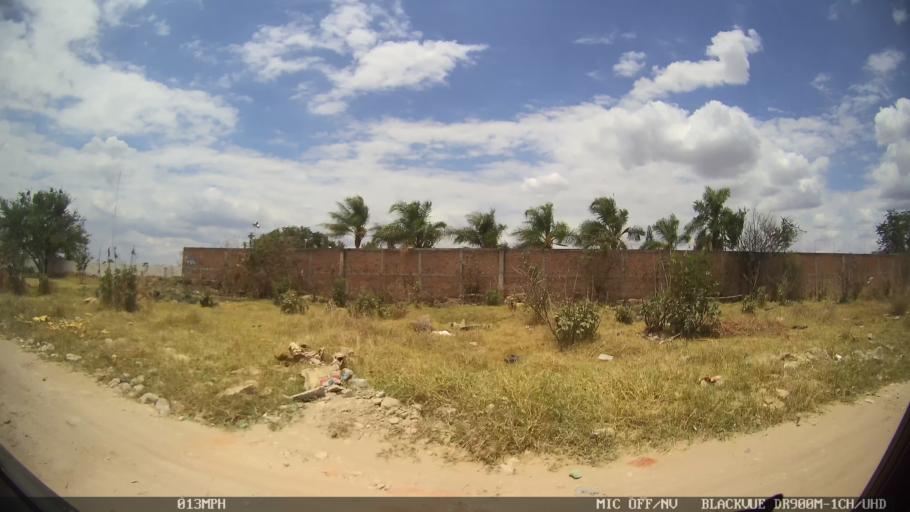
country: MX
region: Jalisco
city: Tlaquepaque
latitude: 20.6395
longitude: -103.2649
